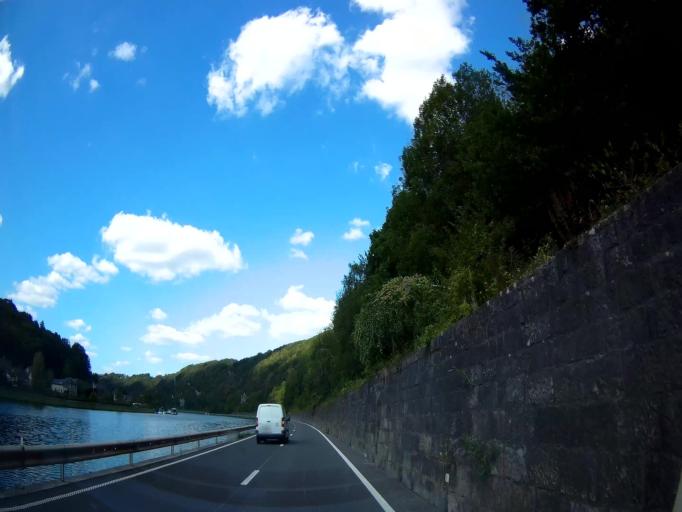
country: BE
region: Wallonia
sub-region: Province de Namur
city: Hastiere-Lavaux
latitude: 50.2094
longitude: 4.8495
